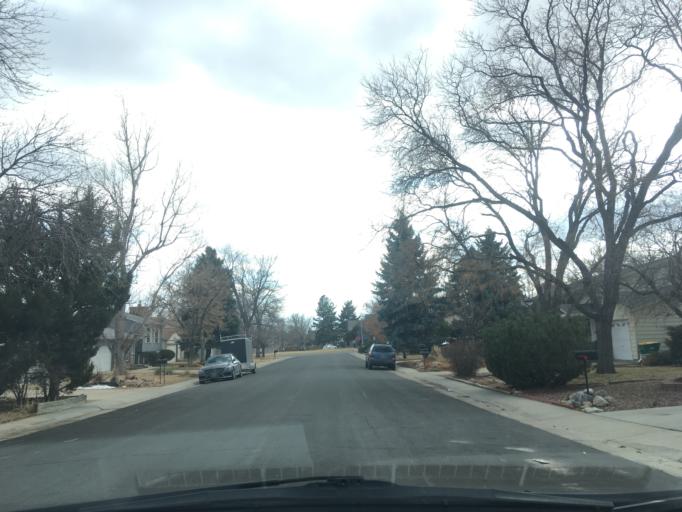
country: US
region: Colorado
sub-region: Broomfield County
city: Broomfield
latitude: 39.9373
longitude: -105.0550
